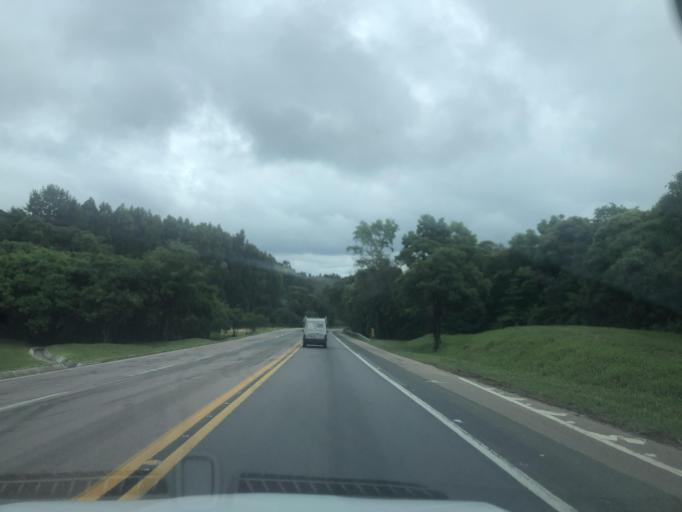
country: BR
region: Parana
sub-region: Araucaria
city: Araucaria
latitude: -25.8651
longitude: -49.3851
